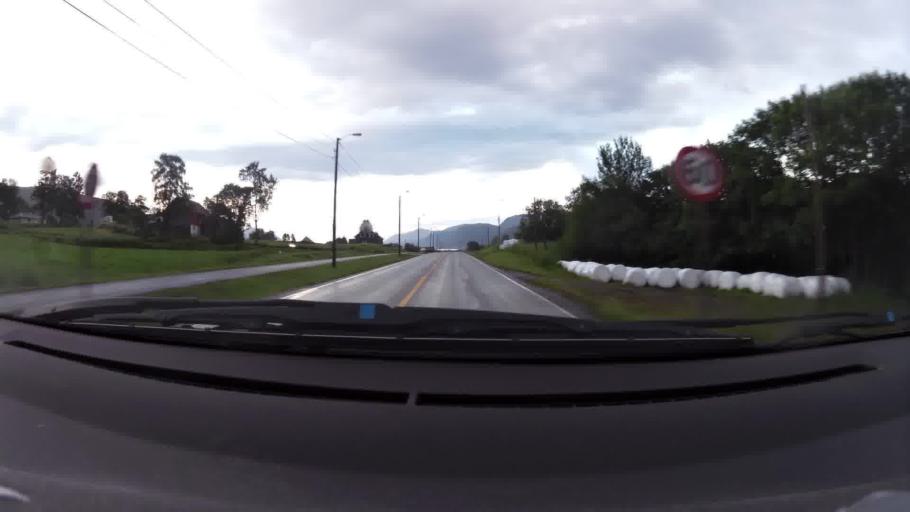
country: NO
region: More og Romsdal
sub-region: Eide
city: Eide
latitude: 62.8933
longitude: 7.3796
